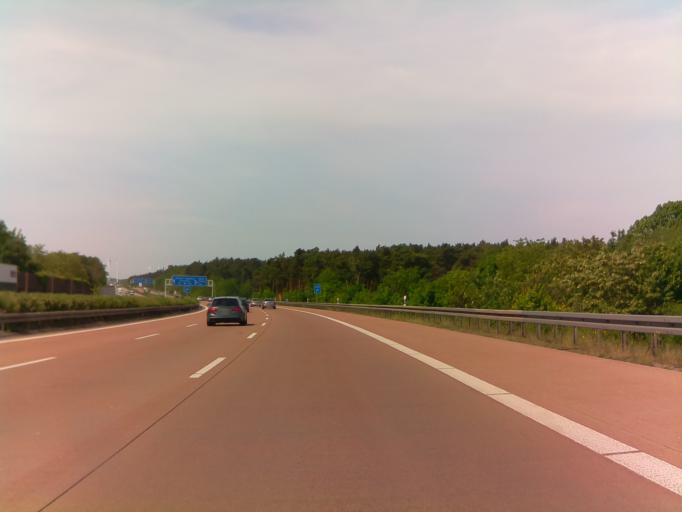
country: DE
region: Brandenburg
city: Gross Kreutz
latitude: 52.3404
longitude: 12.7176
